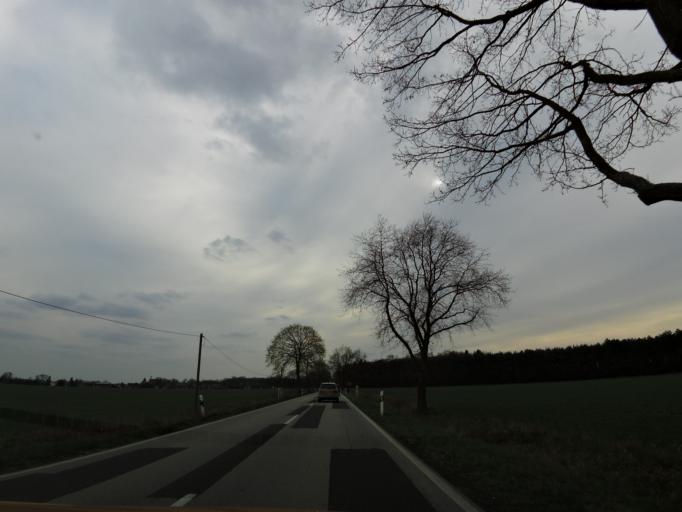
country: DE
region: Brandenburg
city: Beeskow
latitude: 52.2013
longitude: 14.3047
